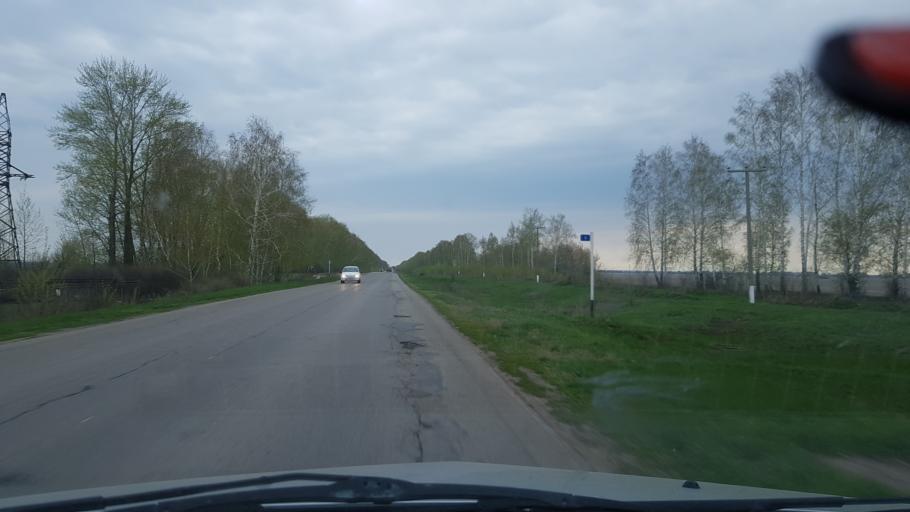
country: RU
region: Samara
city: Podstepki
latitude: 53.6610
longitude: 49.2139
